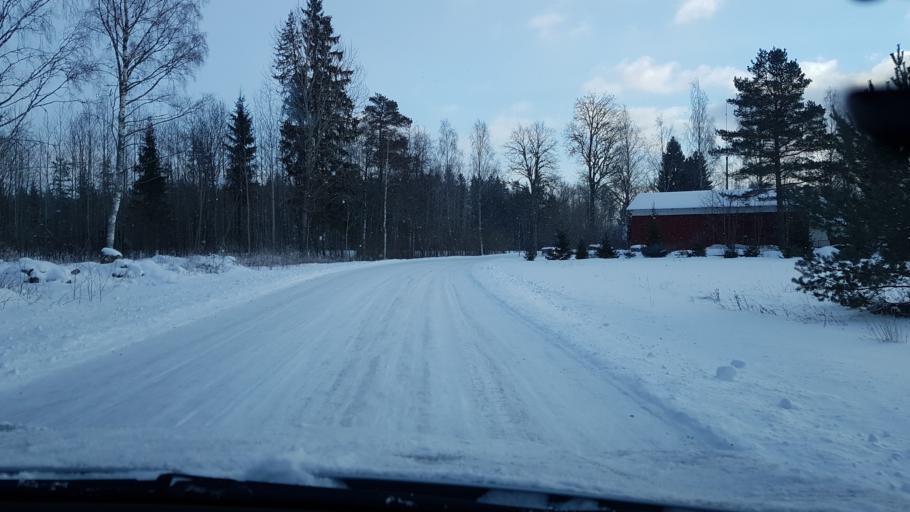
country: EE
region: Harju
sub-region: Nissi vald
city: Turba
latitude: 59.1674
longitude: 24.1404
